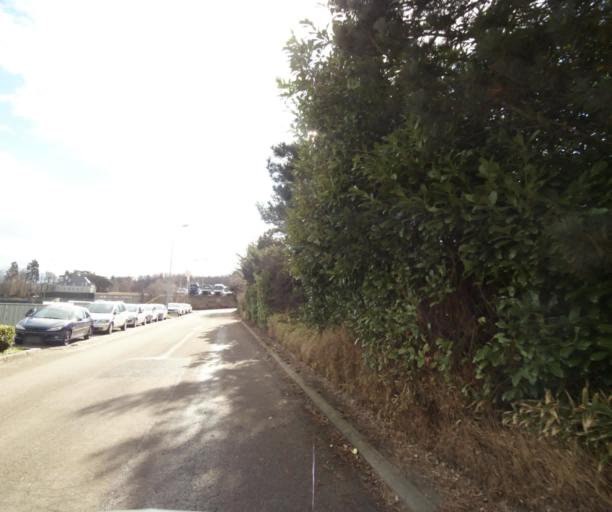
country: FR
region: Rhone-Alpes
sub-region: Departement de la Loire
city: La Talaudiere
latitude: 45.4721
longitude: 4.4229
